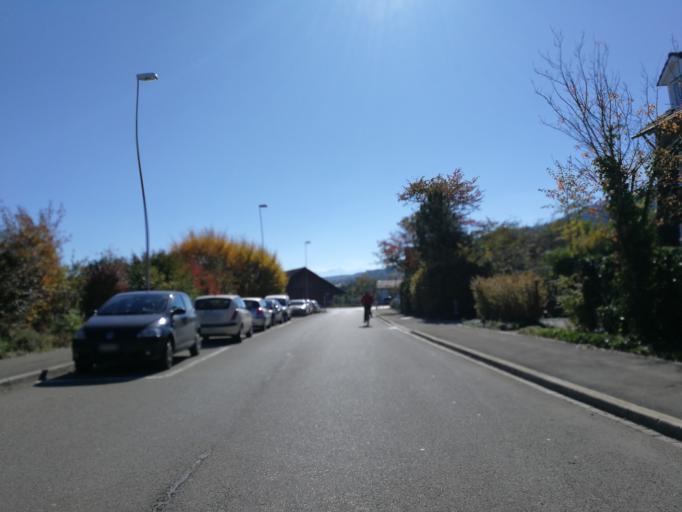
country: CH
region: Zurich
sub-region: Bezirk Uster
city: Egg
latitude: 47.3010
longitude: 8.6877
